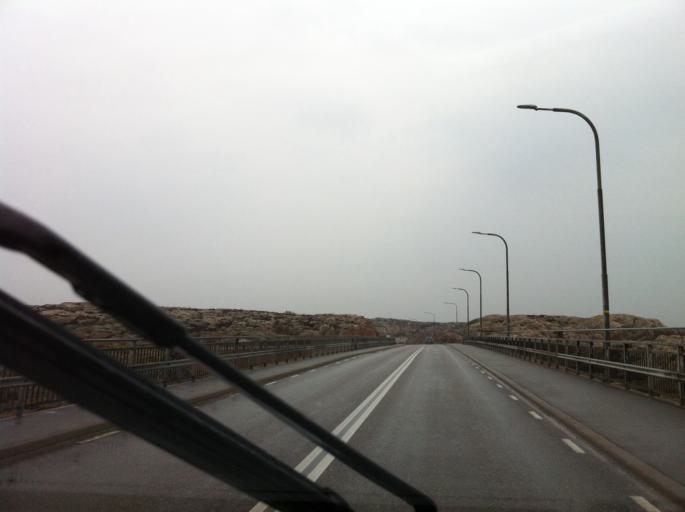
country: SE
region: Vaestra Goetaland
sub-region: Sotenas Kommun
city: Kungshamn
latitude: 58.3650
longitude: 11.2427
